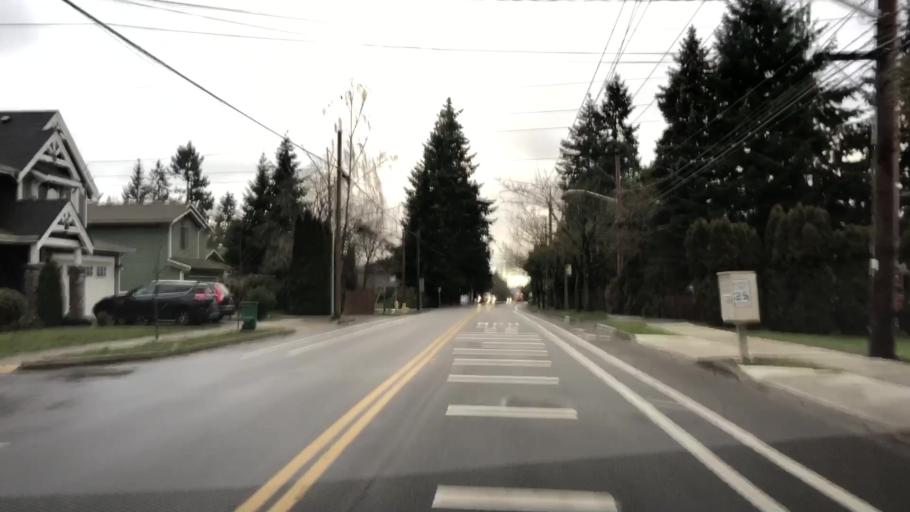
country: US
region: Washington
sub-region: King County
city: Kirkland
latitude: 47.6753
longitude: -122.1736
